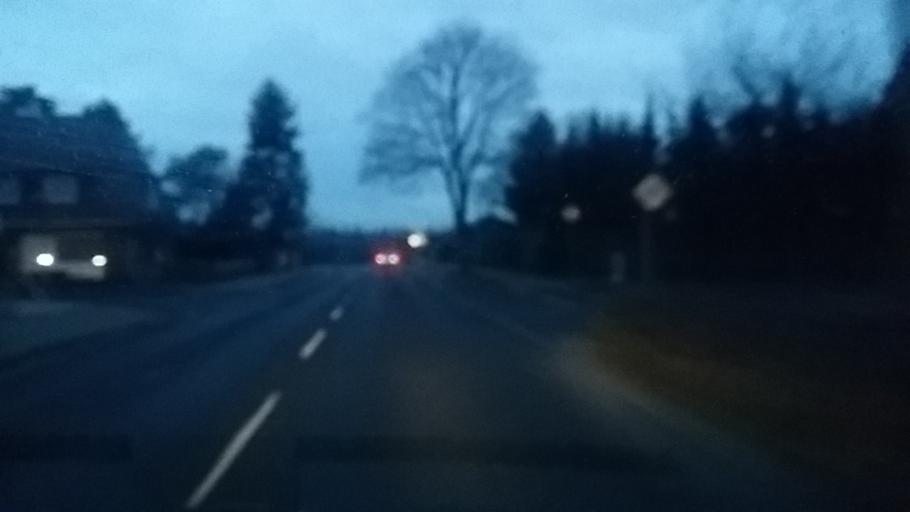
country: DE
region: Lower Saxony
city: Meppen
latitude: 52.7015
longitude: 7.2709
